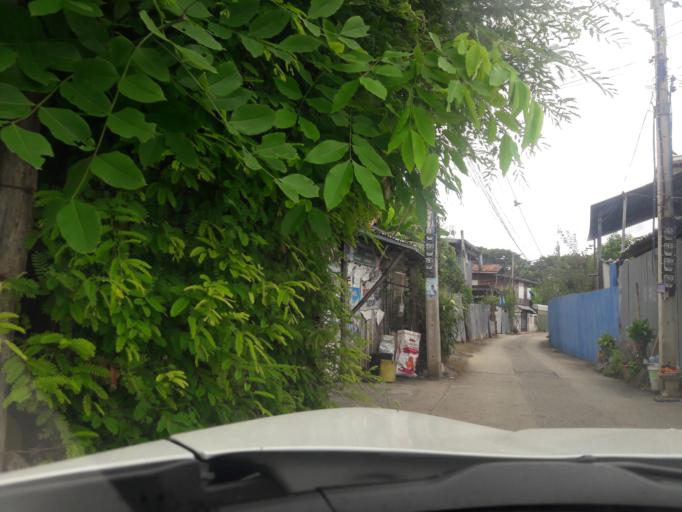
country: TH
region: Lop Buri
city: Ban Mi
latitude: 15.0460
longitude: 100.5457
